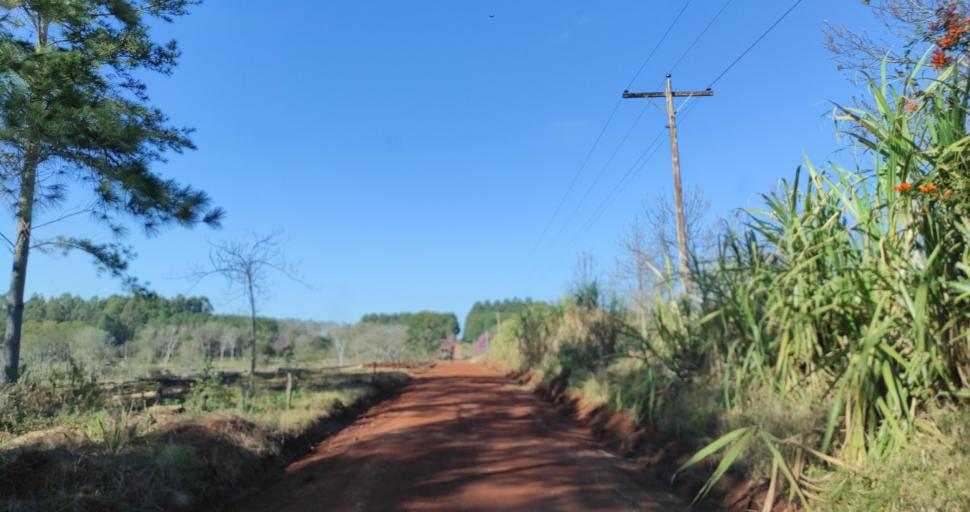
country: AR
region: Misiones
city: Capiovi
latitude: -26.8831
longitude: -55.0373
